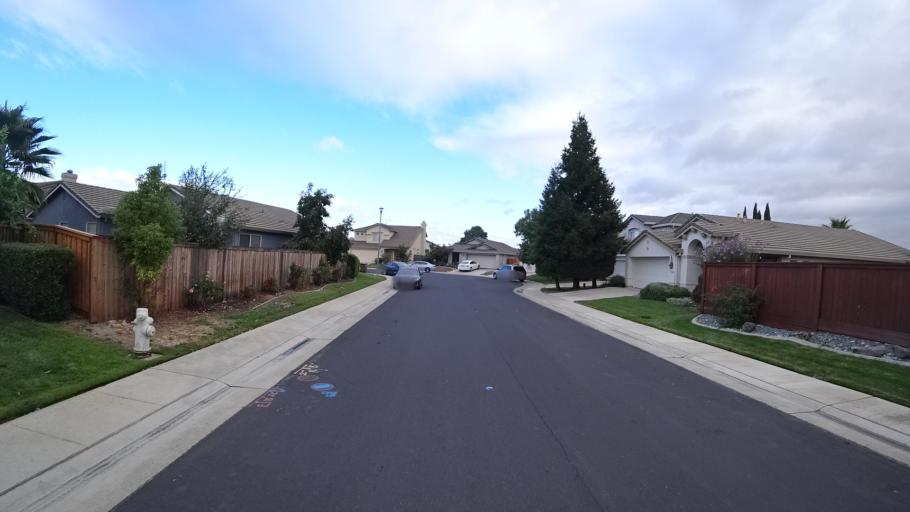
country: US
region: California
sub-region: Sacramento County
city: Laguna
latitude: 38.4320
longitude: -121.4206
